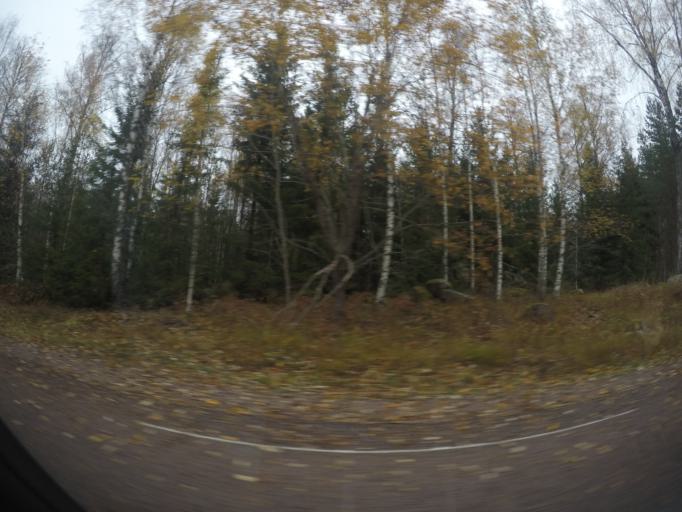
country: SE
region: Vaestmanland
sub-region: Surahammars Kommun
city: Surahammar
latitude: 59.6704
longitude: 16.0785
